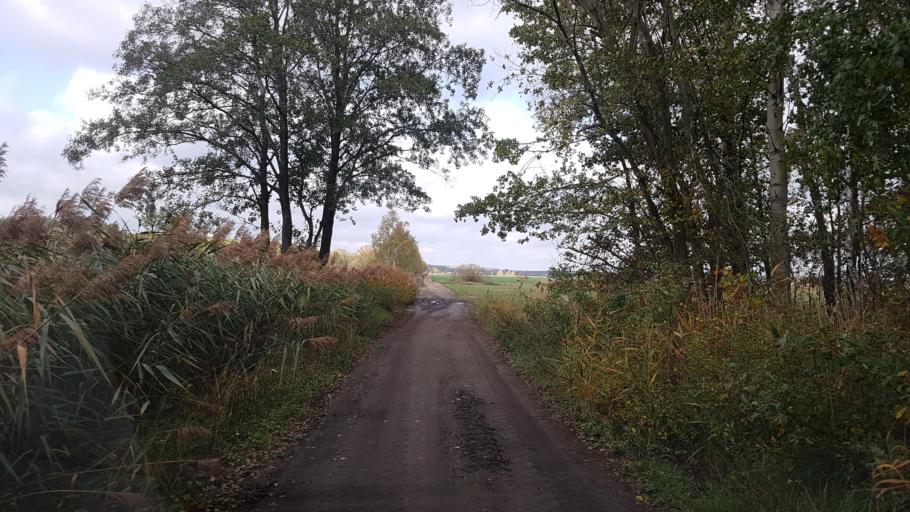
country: DE
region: Brandenburg
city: Schonborn
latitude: 51.5760
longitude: 13.4945
